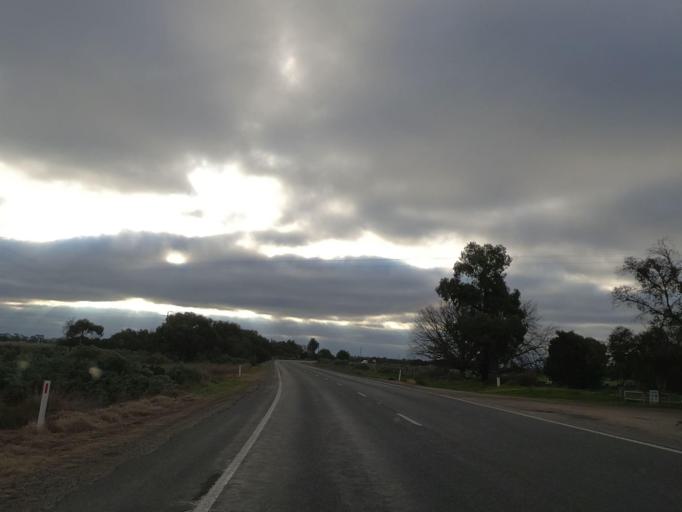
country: AU
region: Victoria
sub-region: Swan Hill
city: Swan Hill
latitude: -35.7234
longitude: 143.8891
